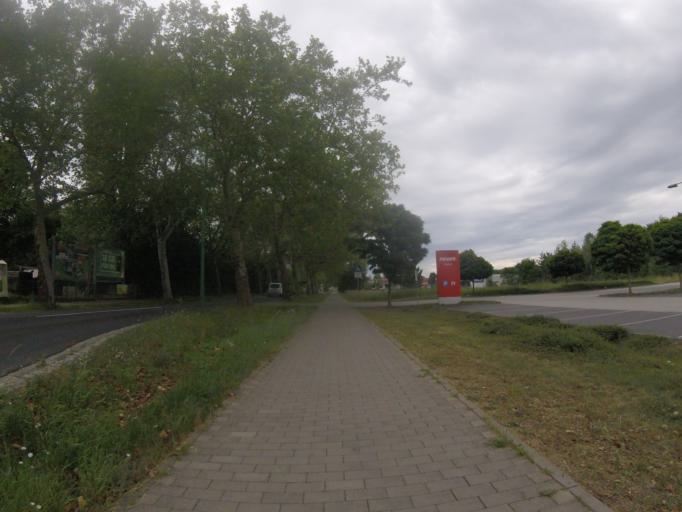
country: DE
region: Brandenburg
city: Konigs Wusterhausen
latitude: 52.2801
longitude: 13.6314
